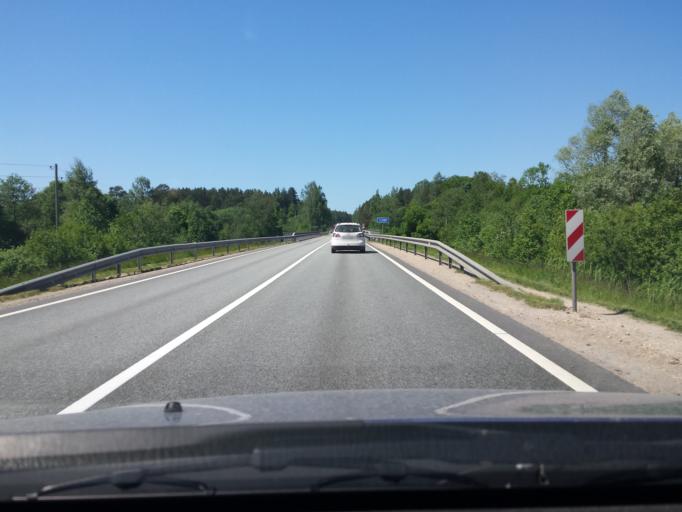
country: LV
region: Riga
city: Bergi
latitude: 56.9764
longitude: 24.3361
